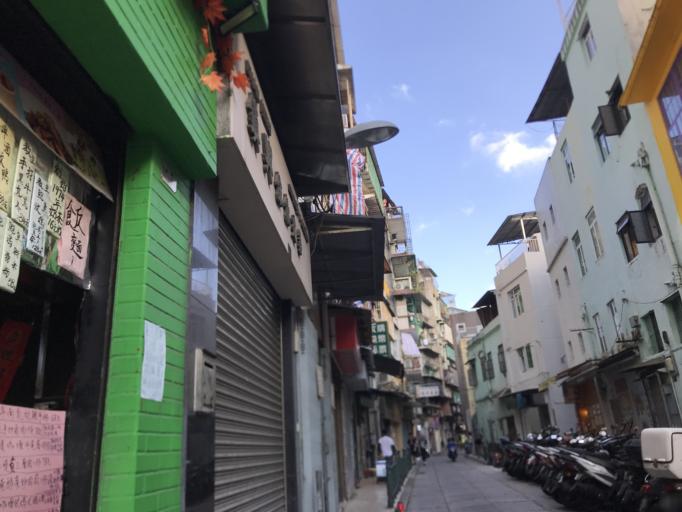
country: MO
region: Macau
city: Macau
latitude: 22.1963
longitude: 113.5399
